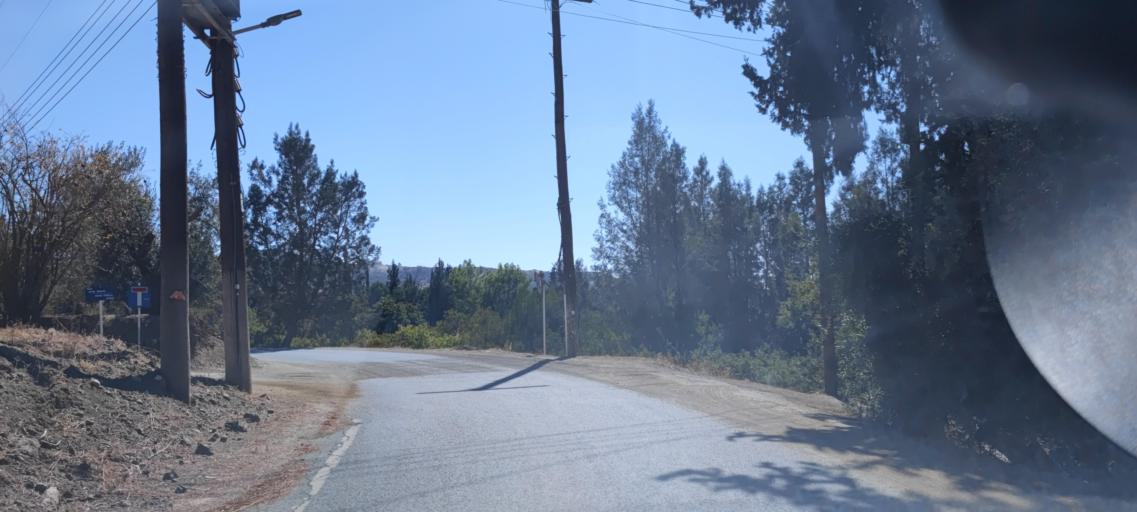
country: CY
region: Limassol
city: Mouttagiaka
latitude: 34.7594
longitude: 33.1061
